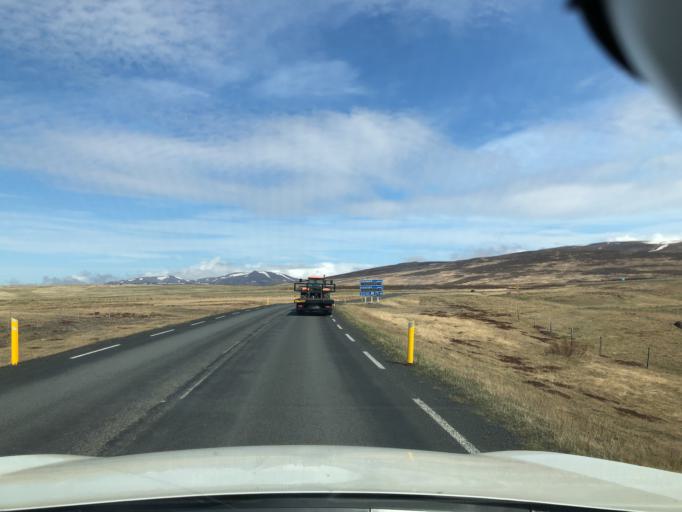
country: IS
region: Northwest
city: Saudarkrokur
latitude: 65.6632
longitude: -20.2628
